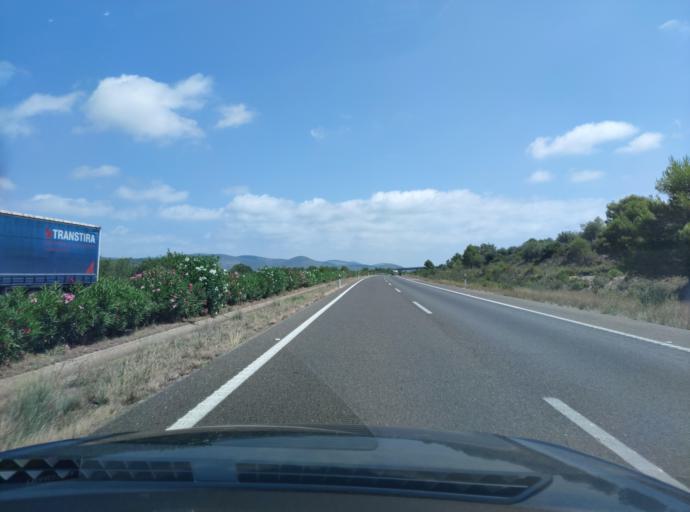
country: ES
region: Valencia
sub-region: Provincia de Castello
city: Santa Magdalena de Pulpis
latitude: 40.3380
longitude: 0.2686
